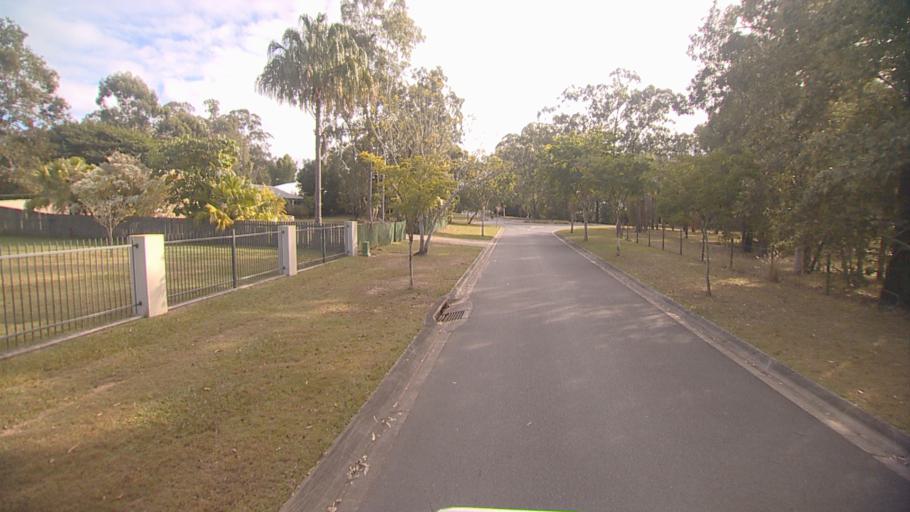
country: AU
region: Queensland
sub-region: Brisbane
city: Forest Lake
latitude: -27.6650
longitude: 152.9932
